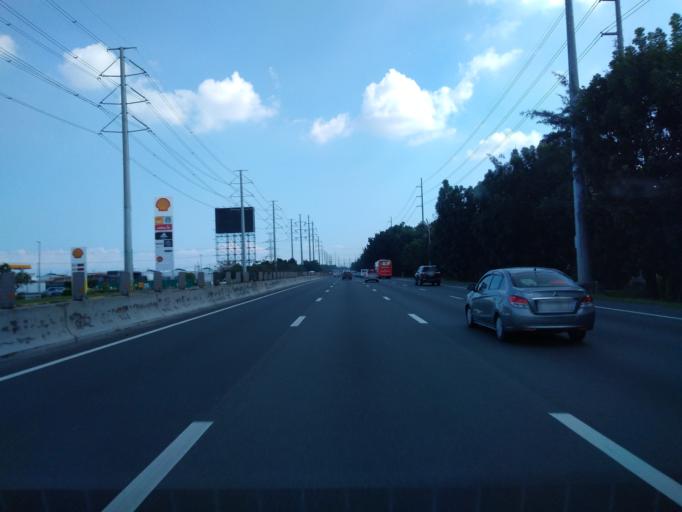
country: PH
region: Calabarzon
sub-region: Province of Cavite
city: Carmona
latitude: 14.3107
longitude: 121.0719
